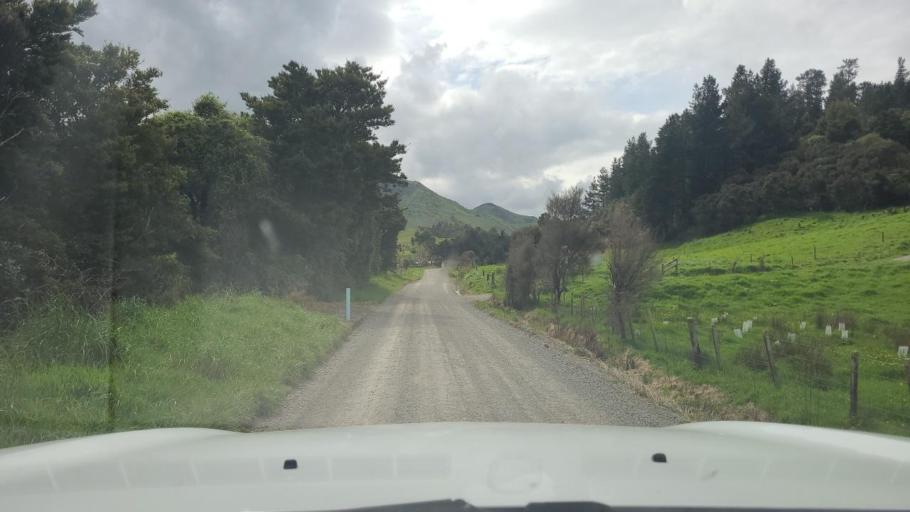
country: NZ
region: Wellington
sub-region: Masterton District
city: Masterton
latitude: -40.9900
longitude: 175.4803
